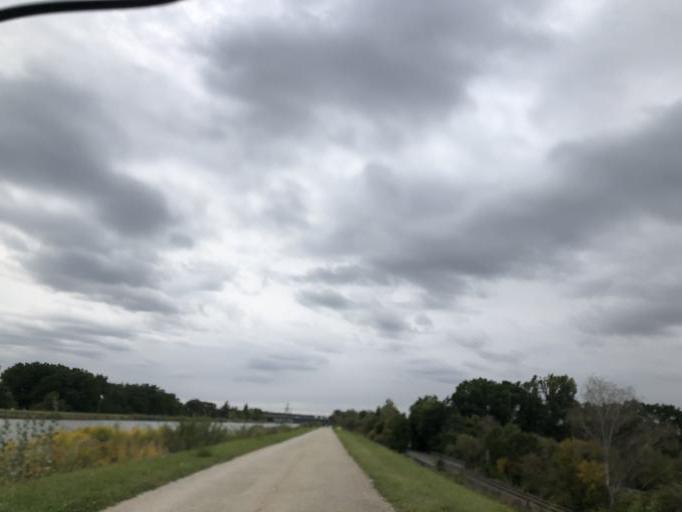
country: DE
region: Bavaria
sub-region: Regierungsbezirk Mittelfranken
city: Erlangen
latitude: 49.5720
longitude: 10.9704
